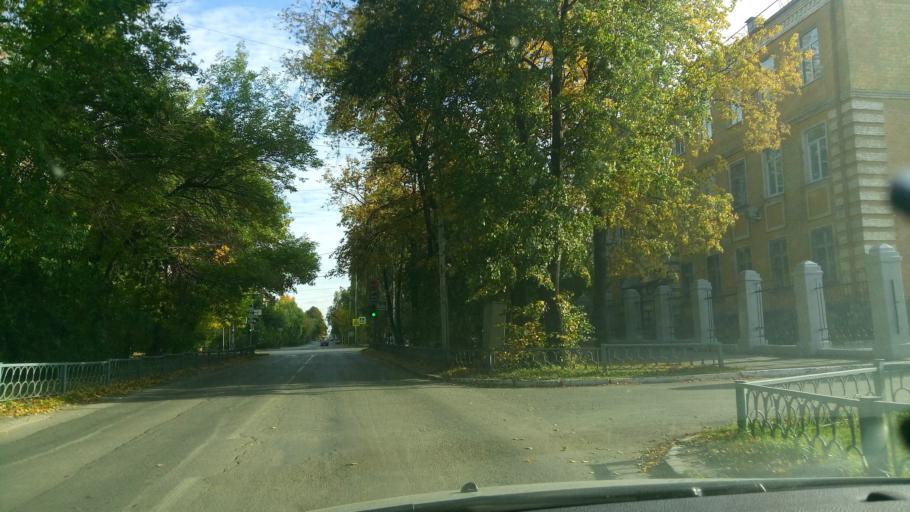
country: RU
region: Sverdlovsk
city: Yekaterinburg
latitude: 56.8901
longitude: 60.6204
